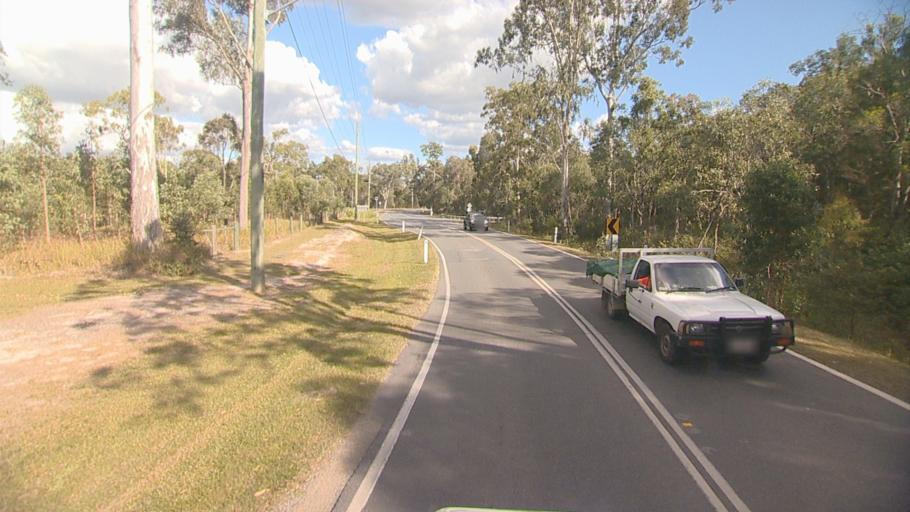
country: AU
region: Queensland
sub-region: Logan
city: Beenleigh
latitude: -27.6568
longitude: 153.2215
